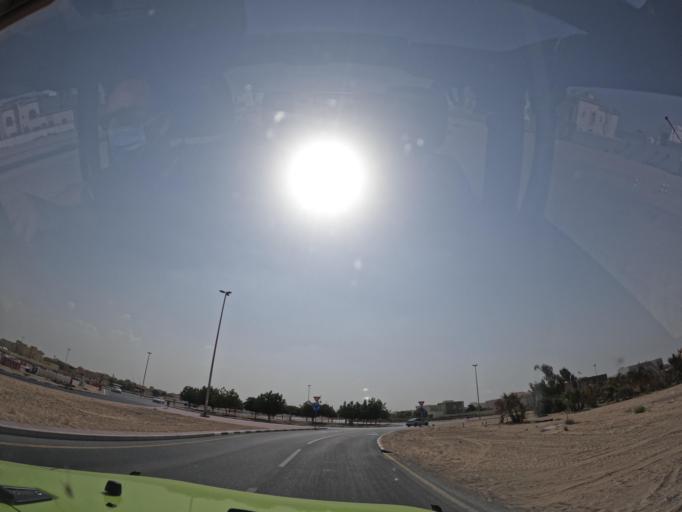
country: AE
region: Ash Shariqah
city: Sharjah
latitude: 25.1850
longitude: 55.4276
